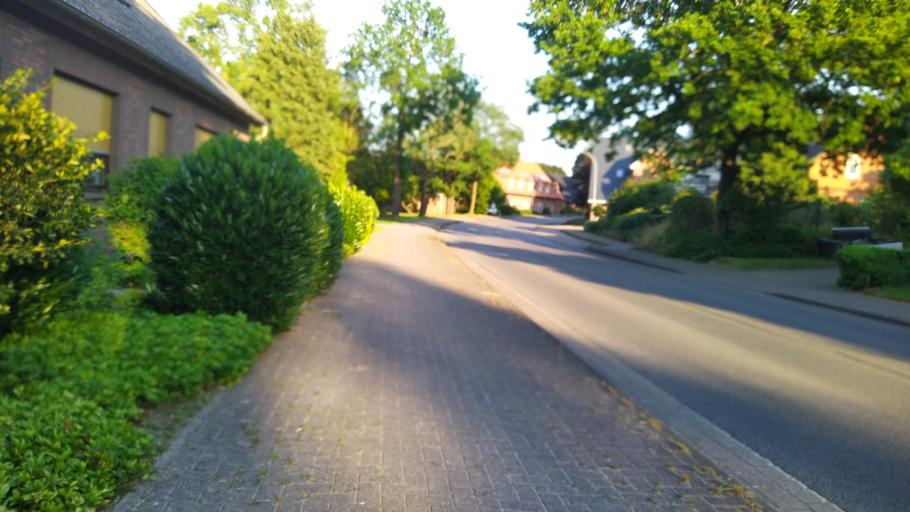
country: DE
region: Lower Saxony
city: Ebersdorf
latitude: 53.5247
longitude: 9.0570
